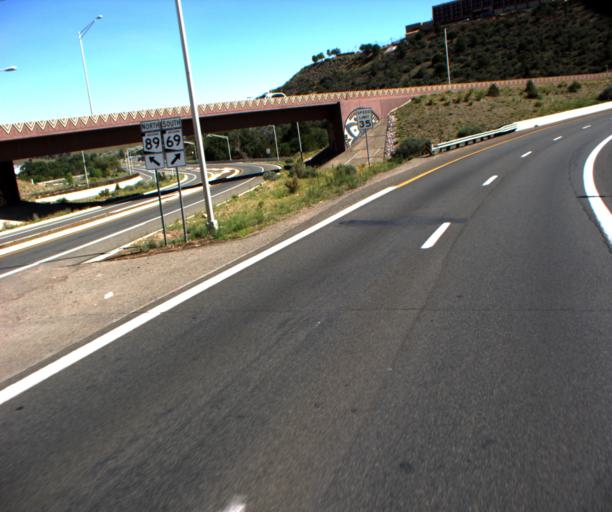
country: US
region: Arizona
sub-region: Yavapai County
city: Prescott
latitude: 34.5474
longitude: -112.4497
